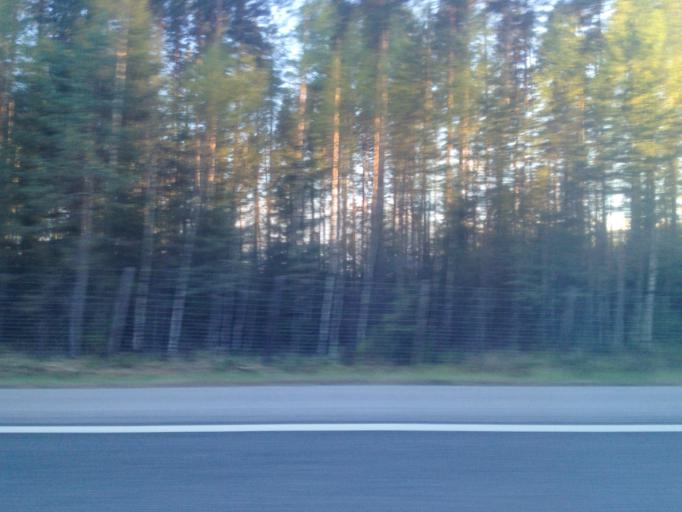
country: FI
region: Haeme
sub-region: Haemeenlinna
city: Janakkala
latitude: 60.9282
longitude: 24.5210
